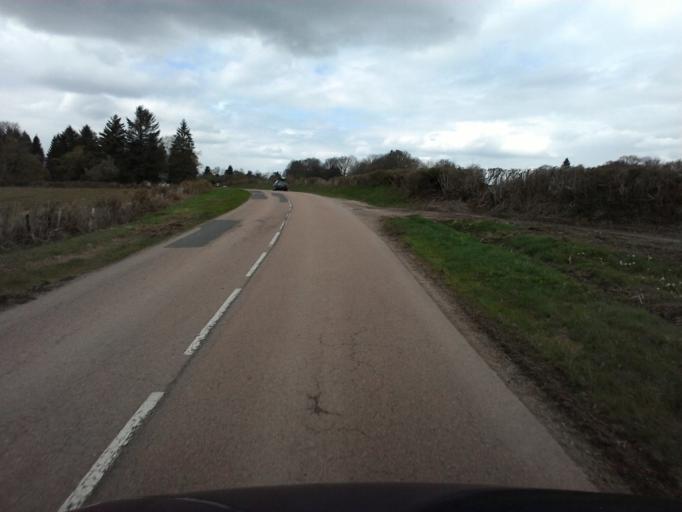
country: FR
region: Bourgogne
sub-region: Departement de la Cote-d'Or
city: Saulieu
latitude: 47.2647
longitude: 4.0293
